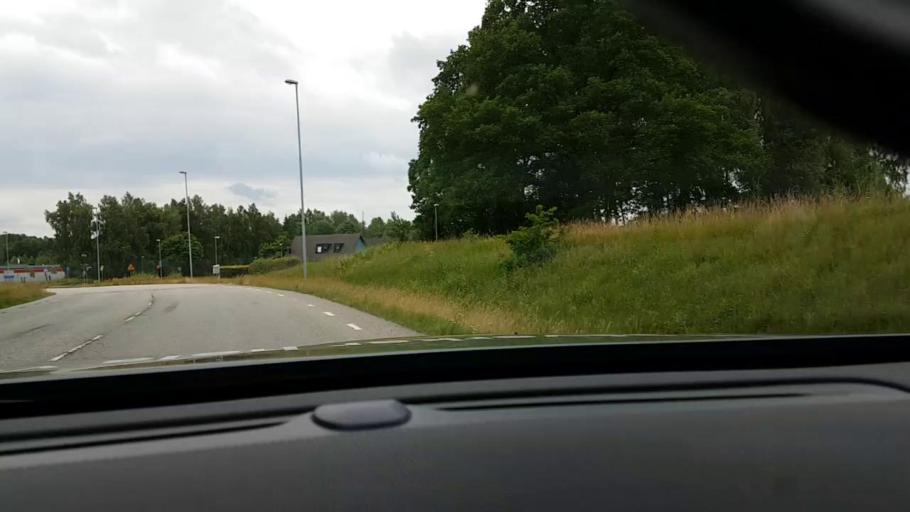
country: SE
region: Skane
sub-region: Hassleholms Kommun
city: Hassleholm
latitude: 56.1709
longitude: 13.8022
